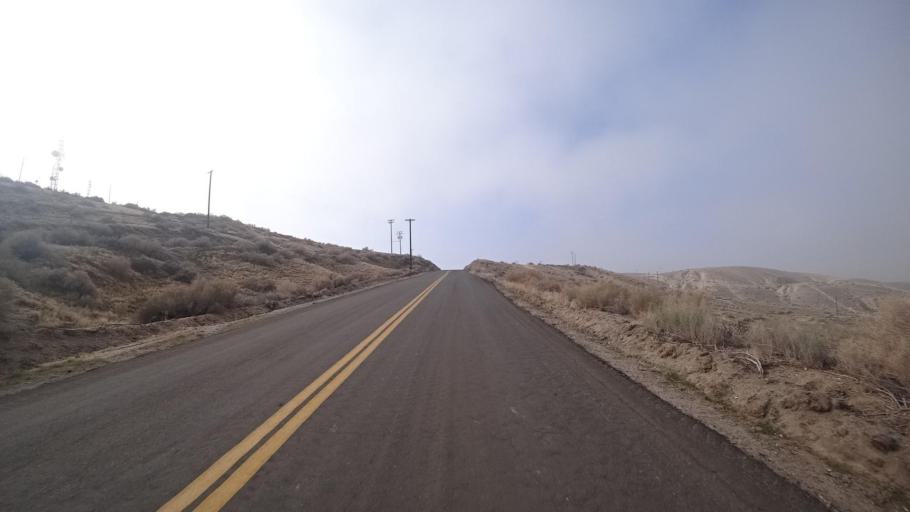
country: US
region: California
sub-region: Kern County
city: Ford City
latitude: 35.1669
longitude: -119.4089
